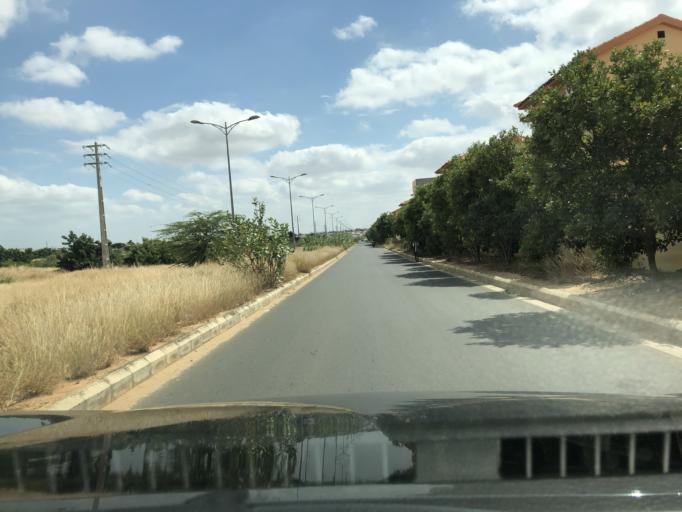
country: AO
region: Luanda
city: Luanda
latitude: -8.9499
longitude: 13.2426
